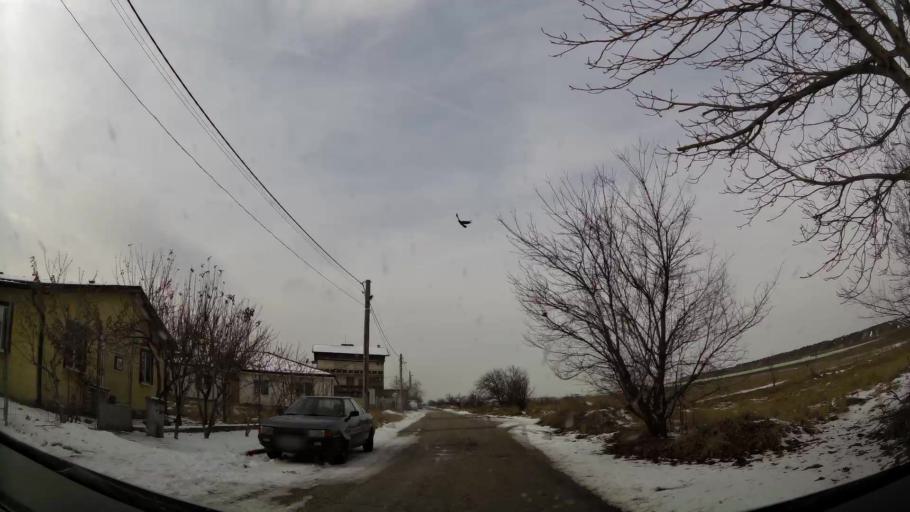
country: BG
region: Sofia-Capital
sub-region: Stolichna Obshtina
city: Sofia
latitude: 42.7168
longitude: 23.4088
